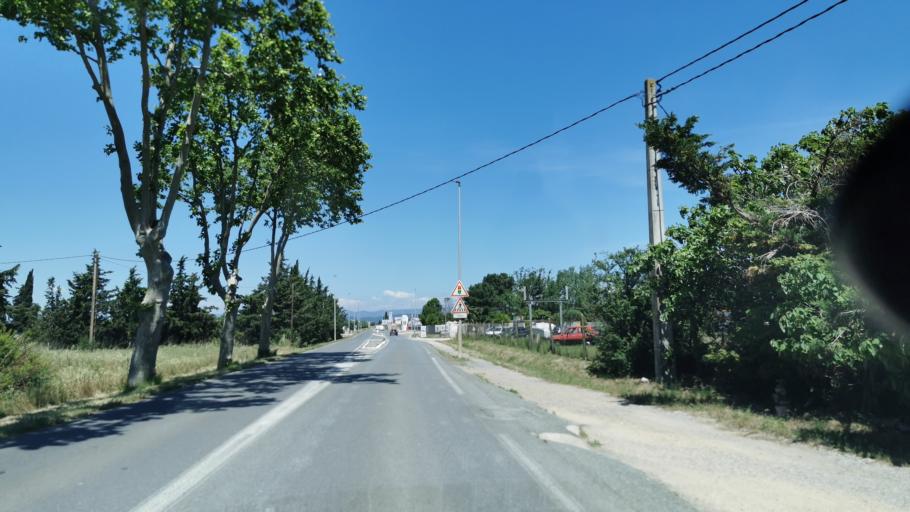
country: FR
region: Languedoc-Roussillon
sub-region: Departement de l'Aude
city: Saint-Marcel-sur-Aude
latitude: 43.2518
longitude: 2.9145
